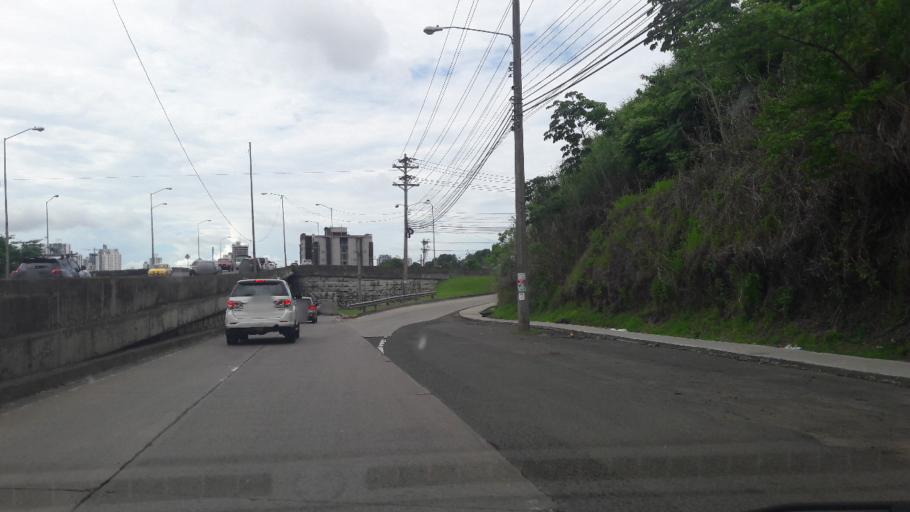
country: PA
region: Panama
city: Panama
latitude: 9.0242
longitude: -79.5278
